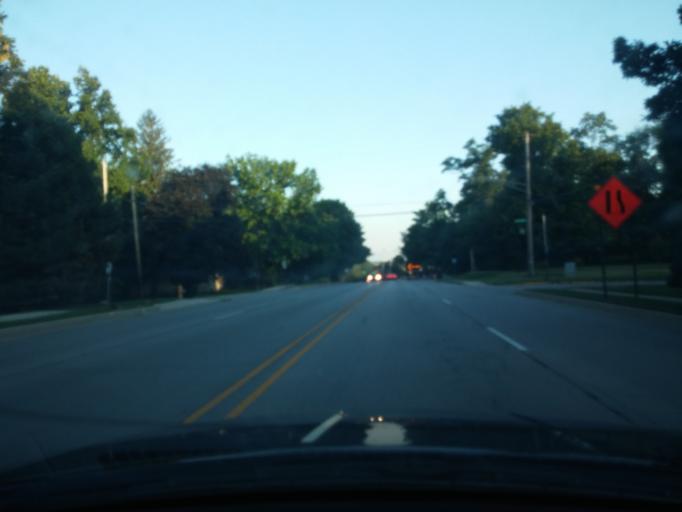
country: US
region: Indiana
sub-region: Tippecanoe County
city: West Lafayette
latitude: 40.4408
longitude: -86.9185
